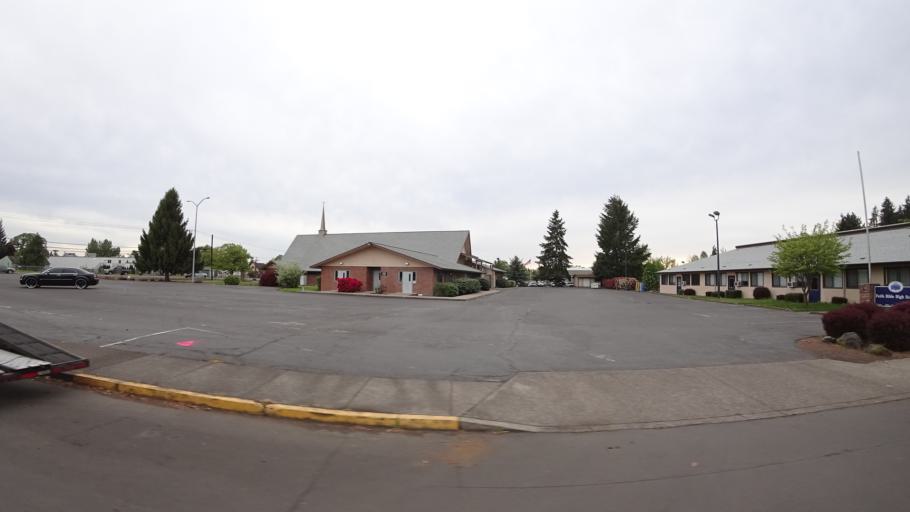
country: US
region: Oregon
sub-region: Washington County
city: Hillsboro
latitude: 45.5019
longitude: -122.9368
